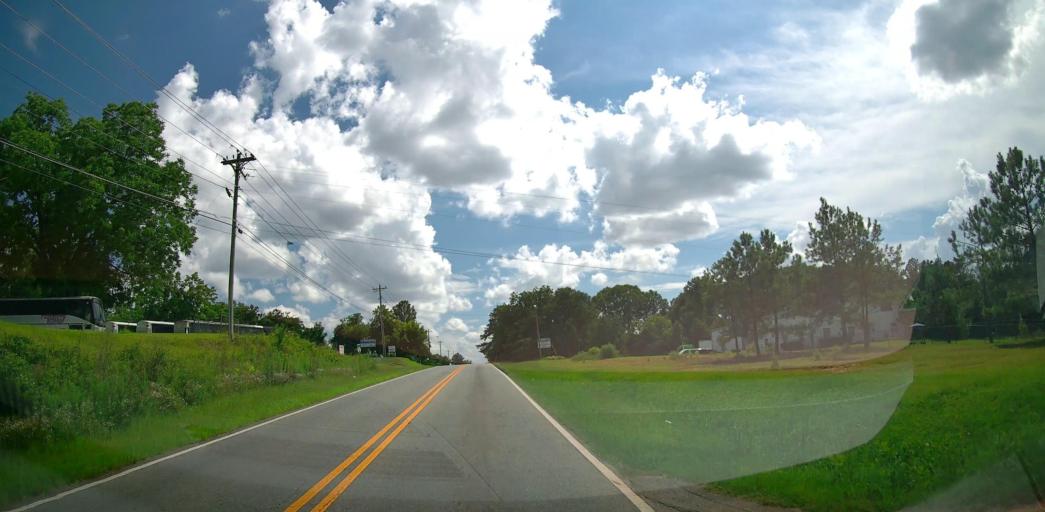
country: US
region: Georgia
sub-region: Houston County
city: Warner Robins
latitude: 32.6568
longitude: -83.6216
